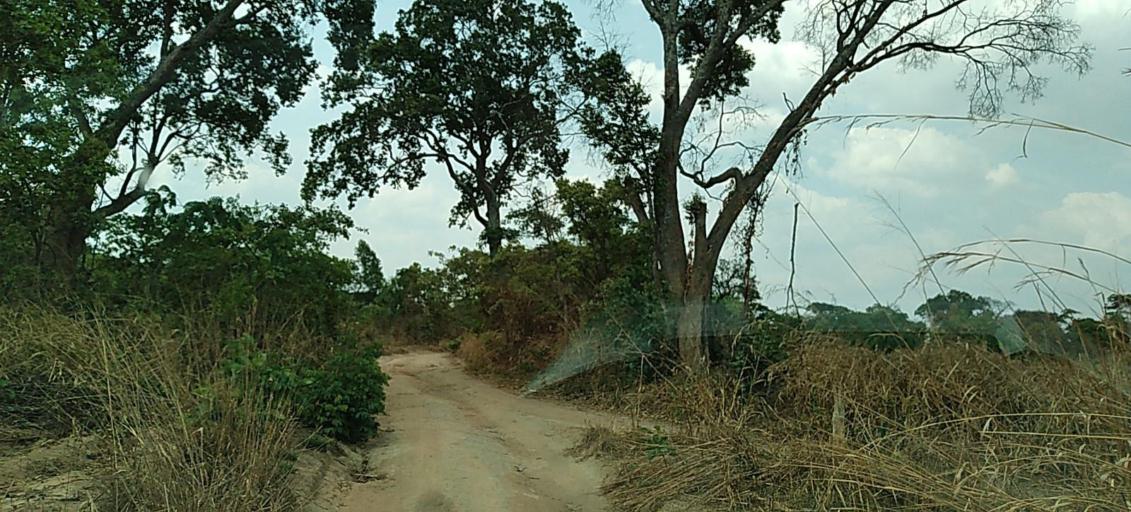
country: ZM
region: Copperbelt
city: Chililabombwe
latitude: -12.3205
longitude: 27.7489
